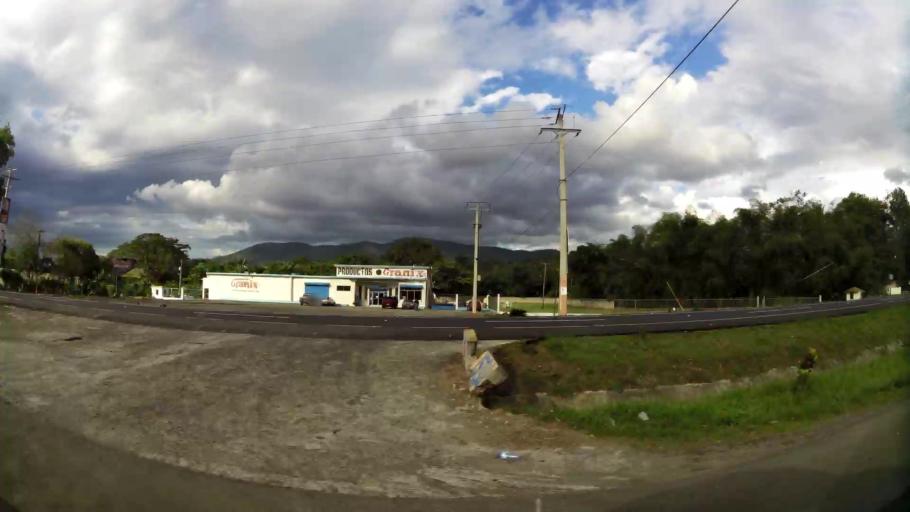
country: DO
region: Monsenor Nouel
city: Piedra Blanca
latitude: 18.8684
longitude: -70.3589
